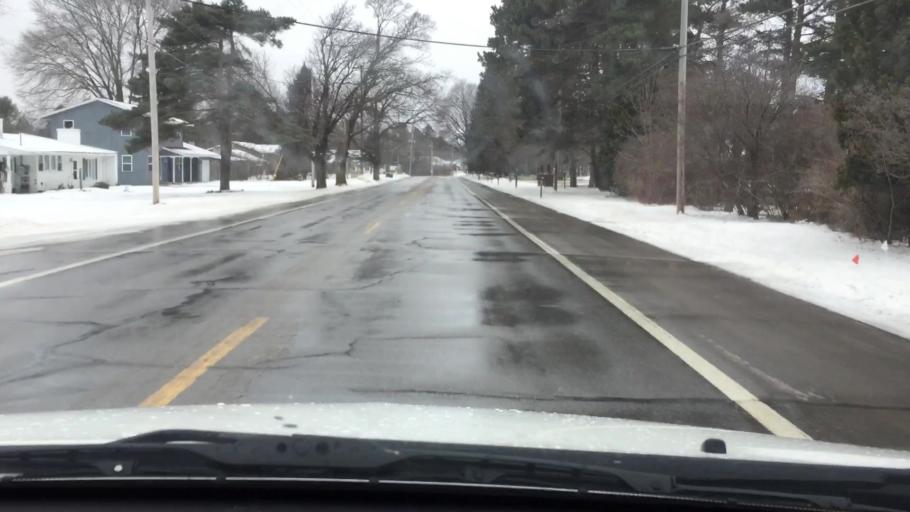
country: US
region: Michigan
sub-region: Wexford County
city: Cadillac
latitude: 44.2339
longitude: -85.4202
